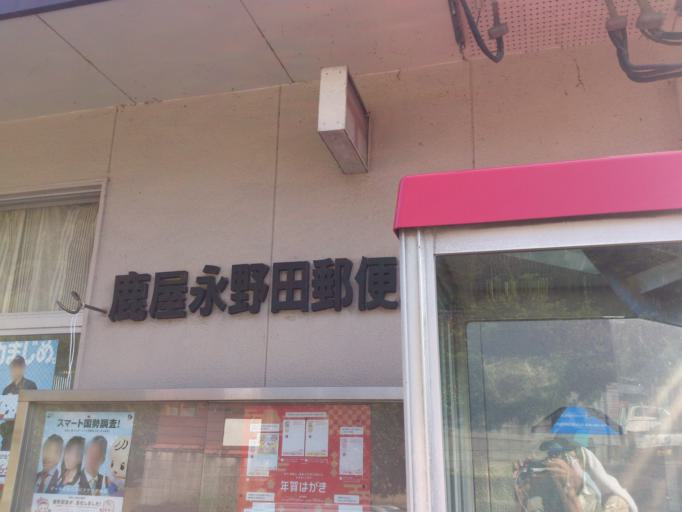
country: JP
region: Kagoshima
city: Kanoya
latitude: 31.3495
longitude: 130.8888
